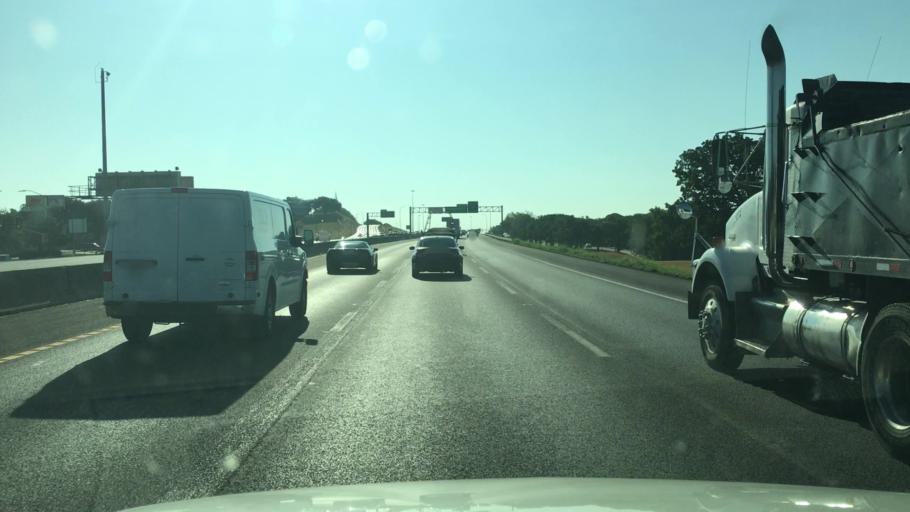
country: US
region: Texas
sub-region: Tarrant County
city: Haltom City
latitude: 32.7605
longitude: -97.2352
